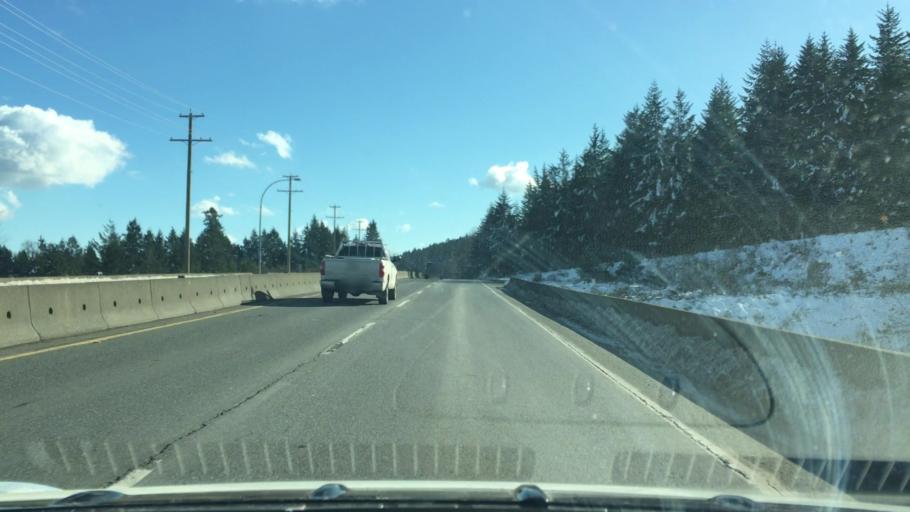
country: CA
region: British Columbia
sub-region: Cowichan Valley Regional District
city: Ladysmith
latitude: 49.0751
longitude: -123.8817
